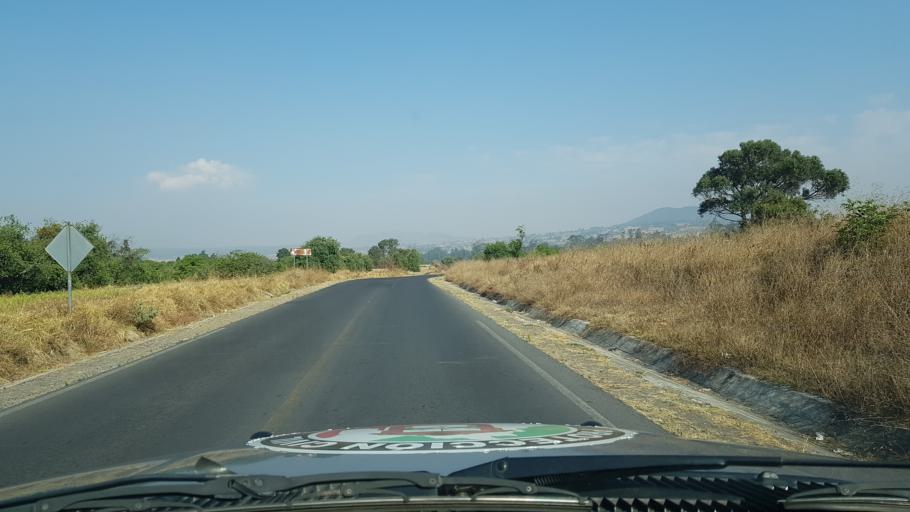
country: MX
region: Mexico
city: Ozumba de Alzate
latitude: 19.0453
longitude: -98.7744
